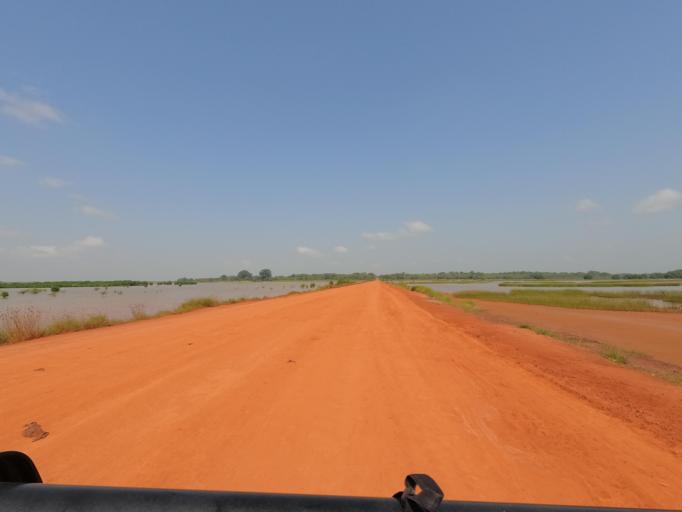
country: GW
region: Cacheu
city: Canchungo
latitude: 12.2587
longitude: -15.7818
